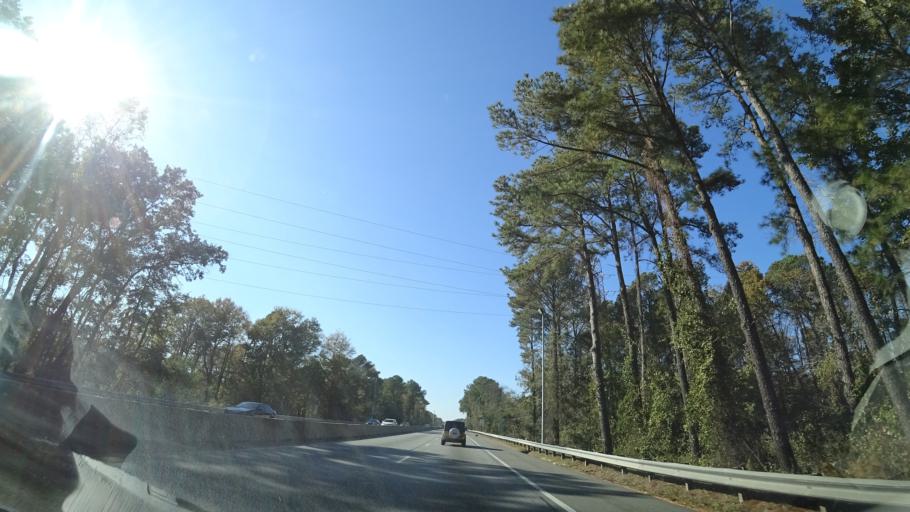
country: US
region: Virginia
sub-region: City of Chesapeake
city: Chesapeake
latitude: 36.7588
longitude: -76.3062
